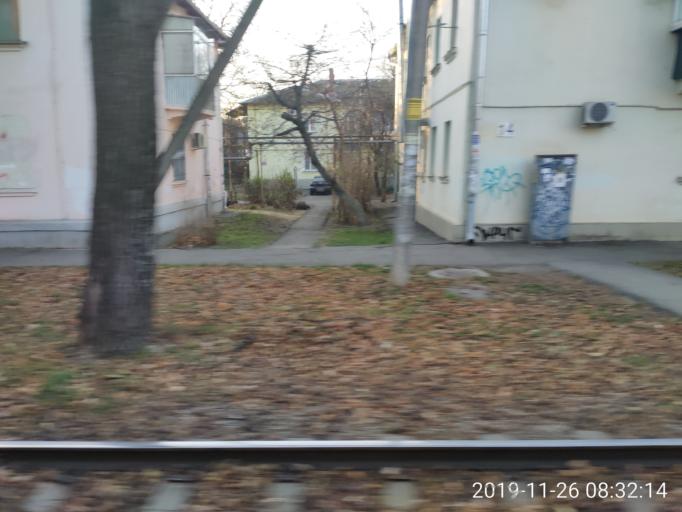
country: RU
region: Krasnodarskiy
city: Krasnodar
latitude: 45.0524
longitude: 38.9952
